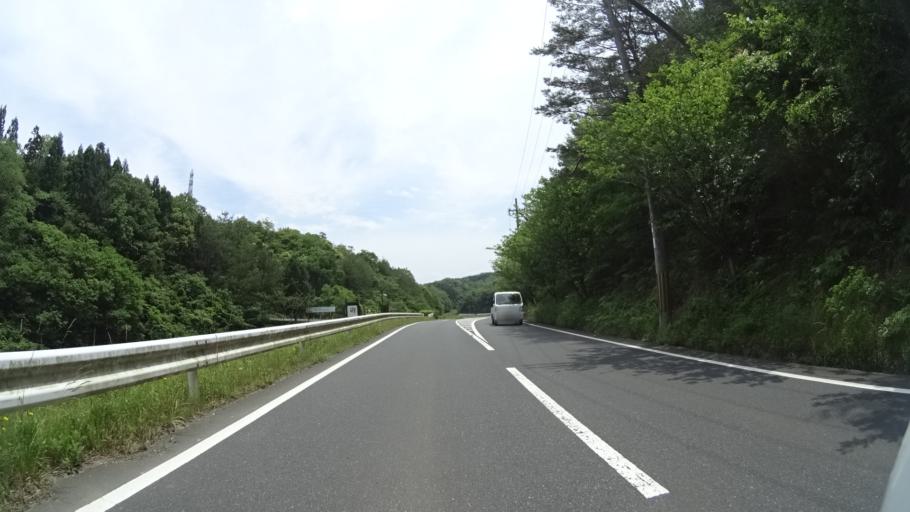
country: JP
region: Kyoto
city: Miyazu
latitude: 35.6737
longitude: 135.0660
